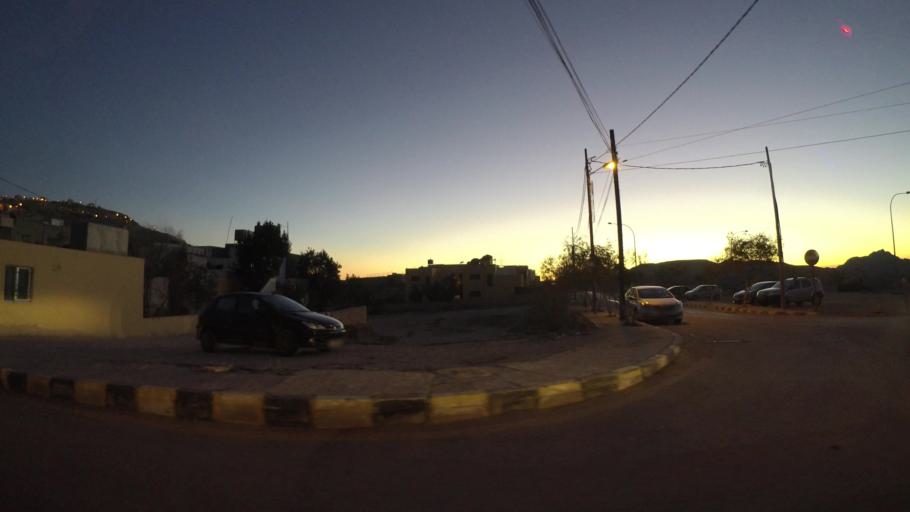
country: JO
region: Ma'an
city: Petra
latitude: 30.3283
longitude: 35.4702
